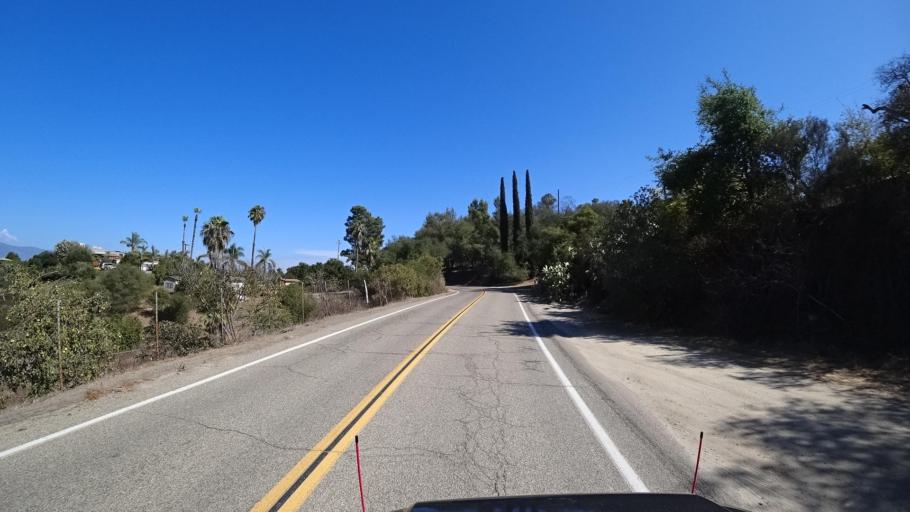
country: US
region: California
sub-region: San Diego County
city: Hidden Meadows
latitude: 33.2954
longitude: -117.1255
